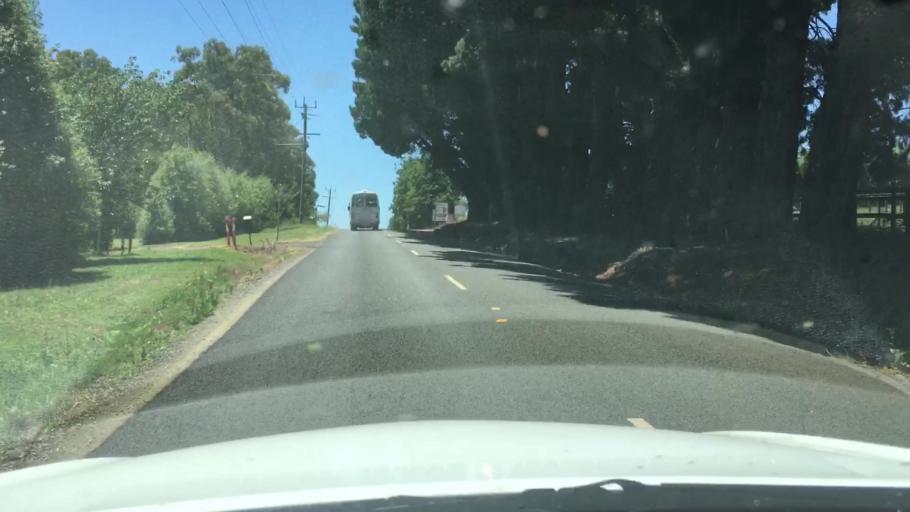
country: AU
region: Victoria
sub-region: Yarra Ranges
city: Mount Evelyn
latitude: -37.7986
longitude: 145.4500
